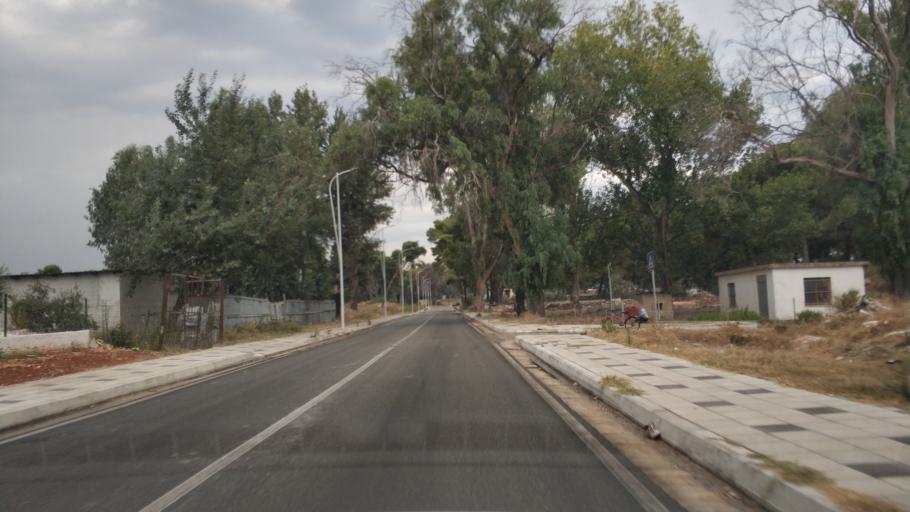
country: AL
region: Vlore
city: Vlore
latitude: 40.4728
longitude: 19.4606
